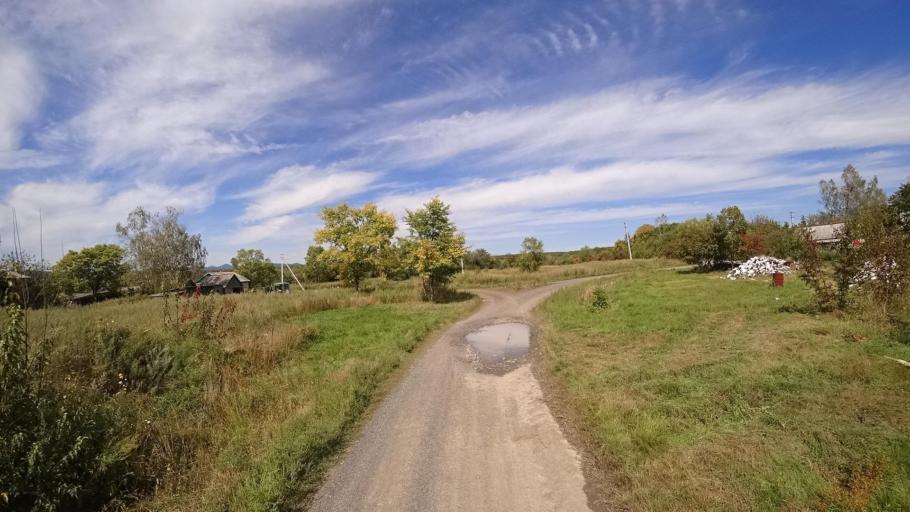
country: RU
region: Primorskiy
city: Yakovlevka
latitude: 44.6417
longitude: 133.5883
